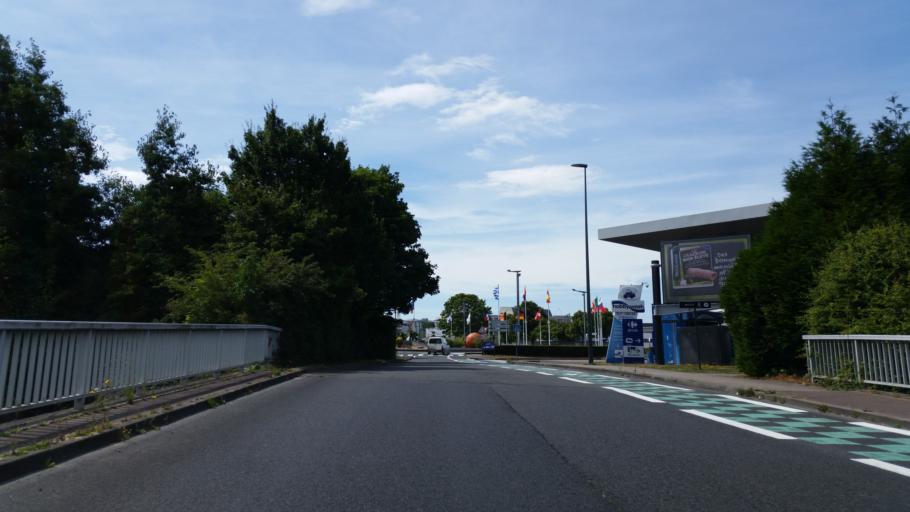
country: FR
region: Lower Normandy
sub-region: Departement du Calvados
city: Herouville-Saint-Clair
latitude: 49.2046
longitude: -0.3265
